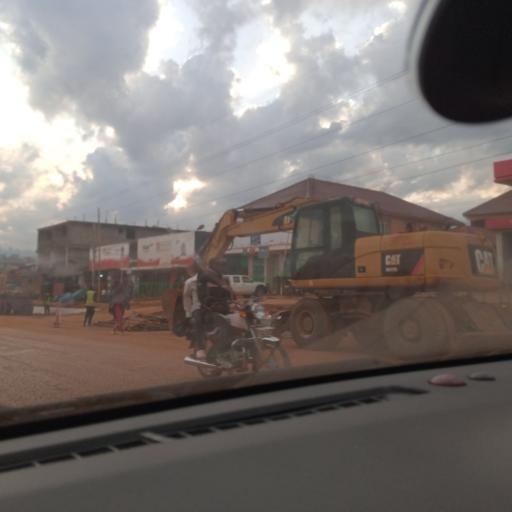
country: UG
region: Central Region
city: Masaka
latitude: -0.3199
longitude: 31.7579
